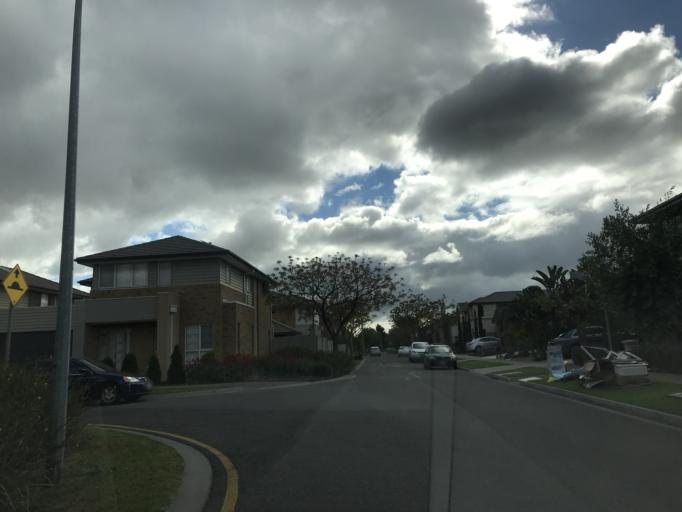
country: AU
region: Victoria
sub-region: Brimbank
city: Sunshine West
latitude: -37.7929
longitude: 144.7933
